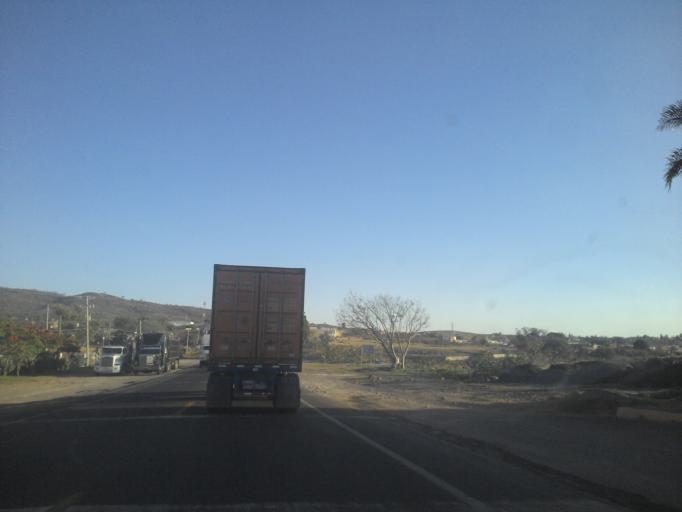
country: MX
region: Jalisco
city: Zapotlanejo
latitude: 20.6334
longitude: -103.0514
